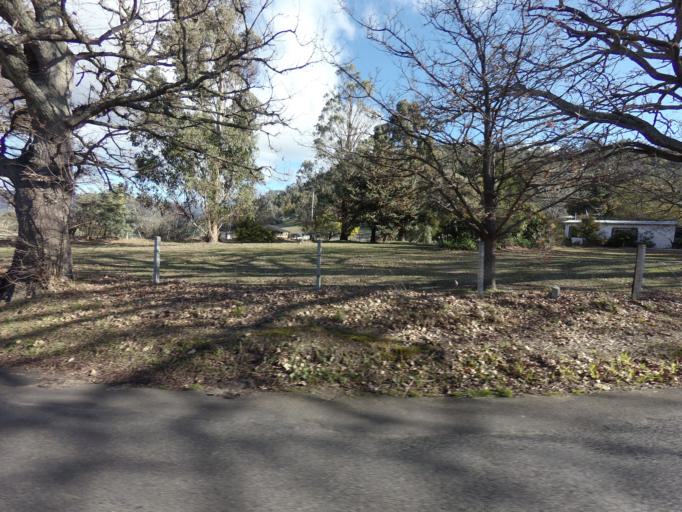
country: AU
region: Tasmania
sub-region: Derwent Valley
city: New Norfolk
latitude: -42.7491
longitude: 147.0461
